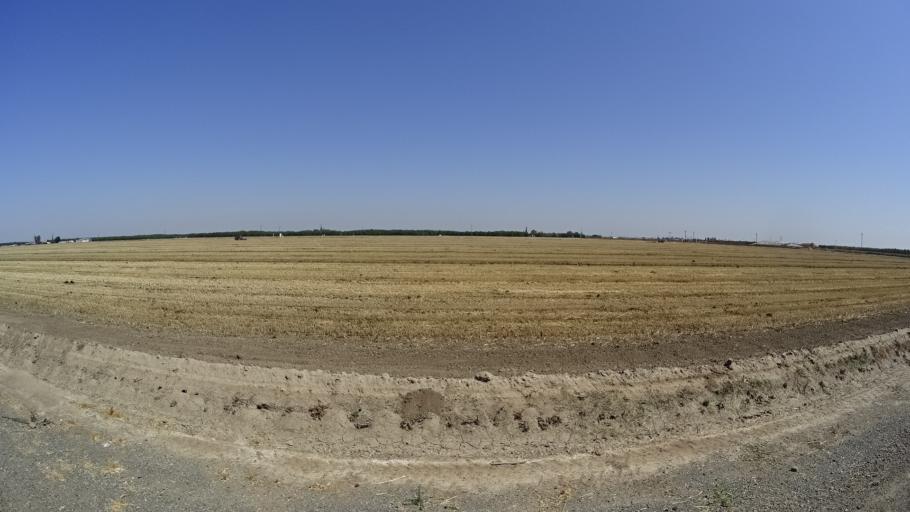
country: US
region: California
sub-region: Kings County
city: Lucerne
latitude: 36.3717
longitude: -119.7024
